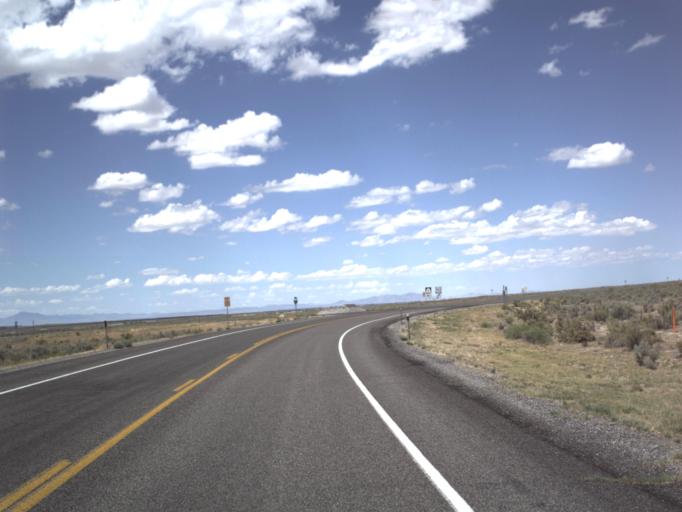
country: US
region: Utah
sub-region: Millard County
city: Fillmore
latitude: 39.1544
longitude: -112.4056
